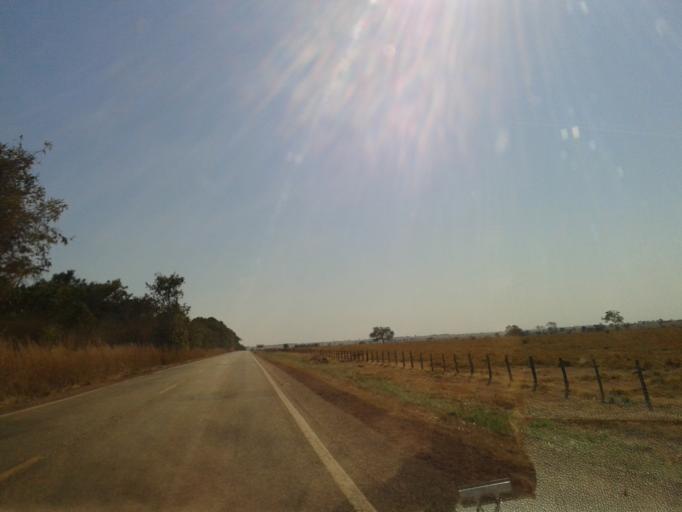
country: BR
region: Goias
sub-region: Mozarlandia
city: Mozarlandia
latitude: -14.3900
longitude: -50.4384
